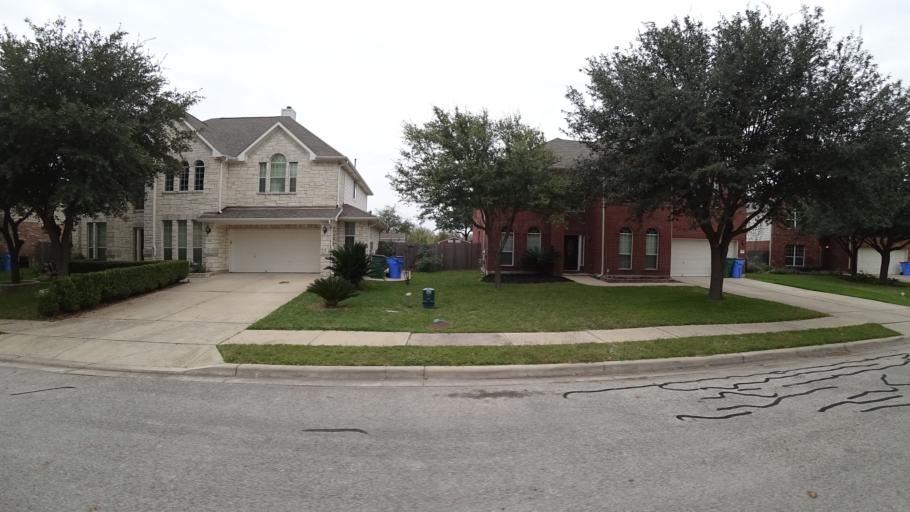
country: US
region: Texas
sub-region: Travis County
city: Pflugerville
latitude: 30.4537
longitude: -97.6229
